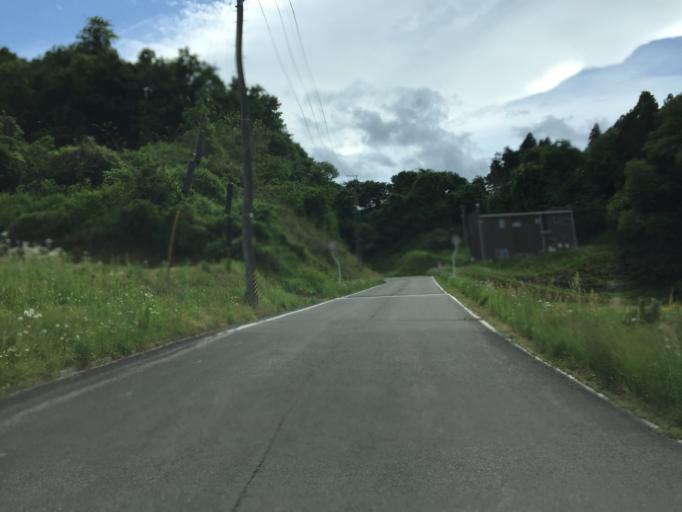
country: JP
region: Fukushima
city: Nihommatsu
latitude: 37.6220
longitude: 140.5129
